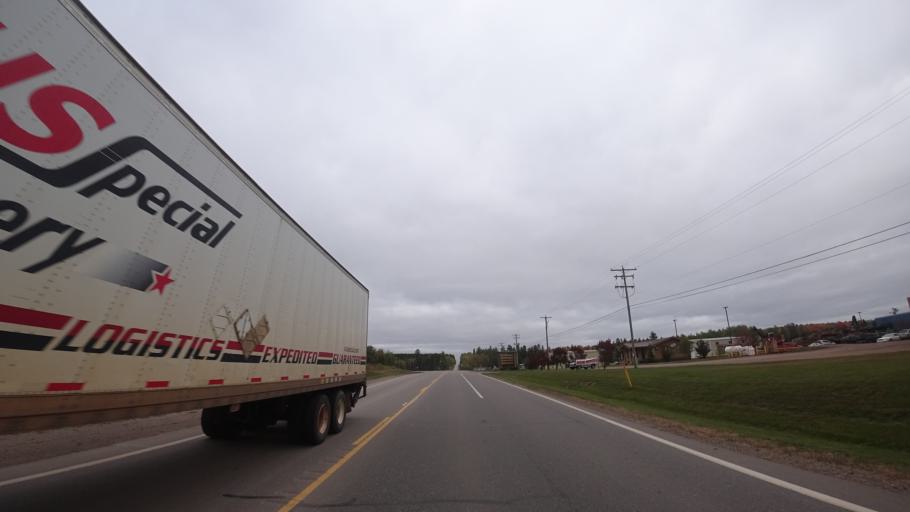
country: US
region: Wisconsin
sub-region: Florence County
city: Florence
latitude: 46.1066
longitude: -88.0758
